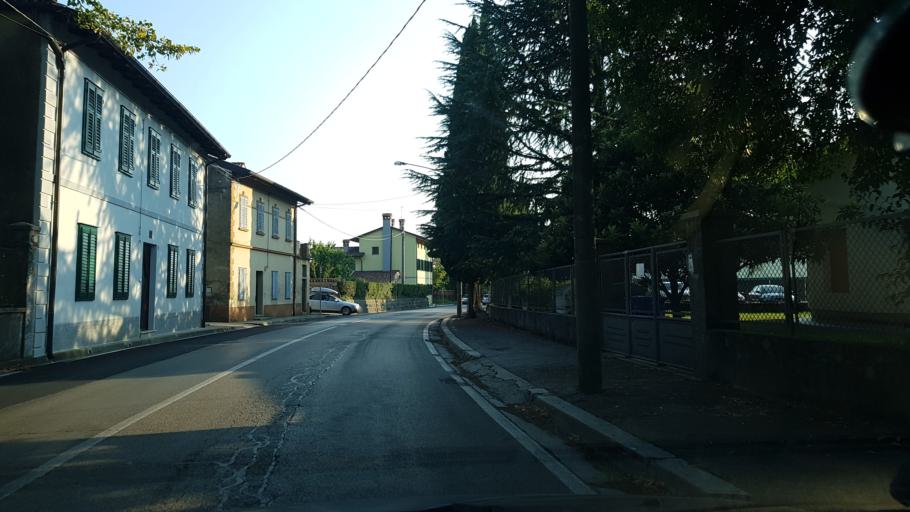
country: IT
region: Friuli Venezia Giulia
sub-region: Provincia di Gorizia
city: Gorizia
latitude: 45.9622
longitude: 13.6151
